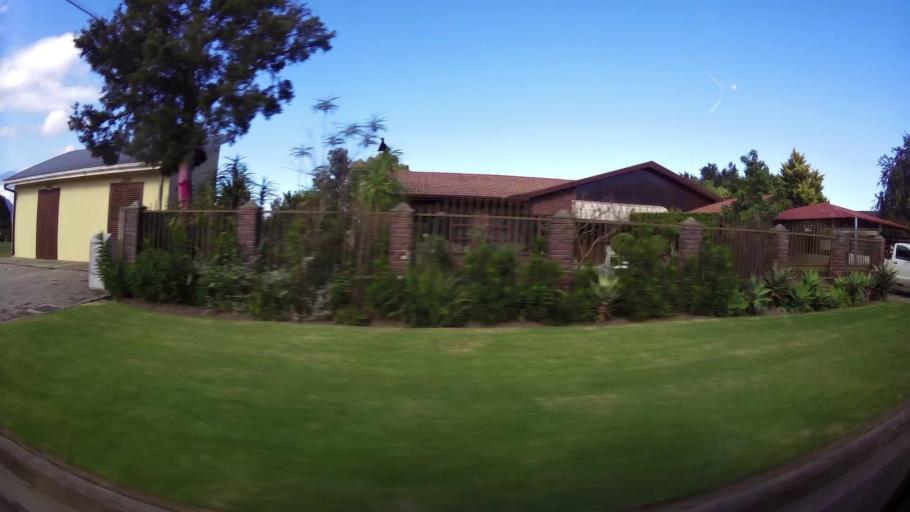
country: ZA
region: Western Cape
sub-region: Eden District Municipality
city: George
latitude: -33.9642
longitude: 22.4872
